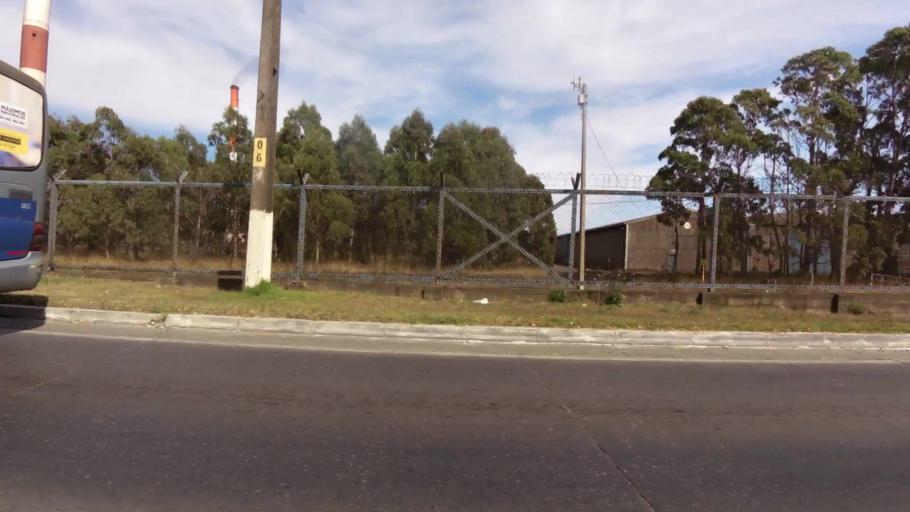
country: CL
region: Biobio
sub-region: Provincia de Concepcion
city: Talcahuano
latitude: -36.7376
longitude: -73.1208
